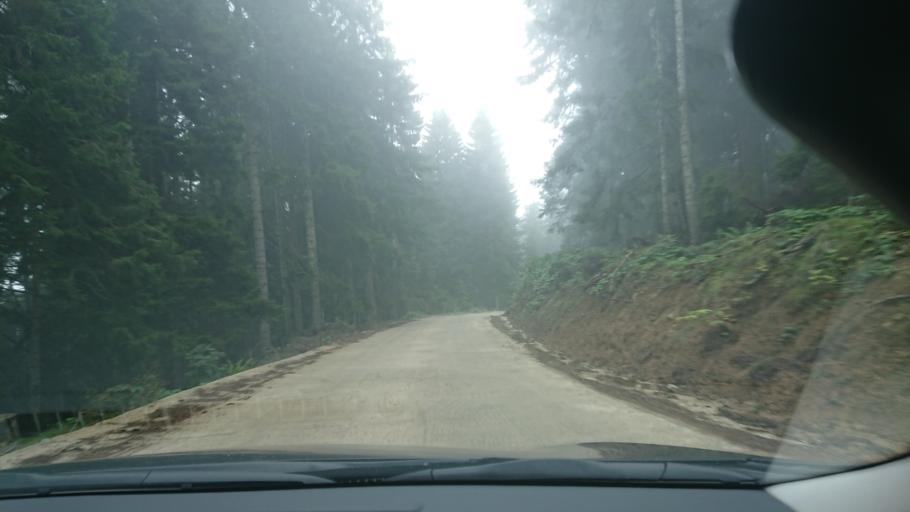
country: TR
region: Gumushane
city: Kurtun
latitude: 40.6648
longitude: 39.0132
